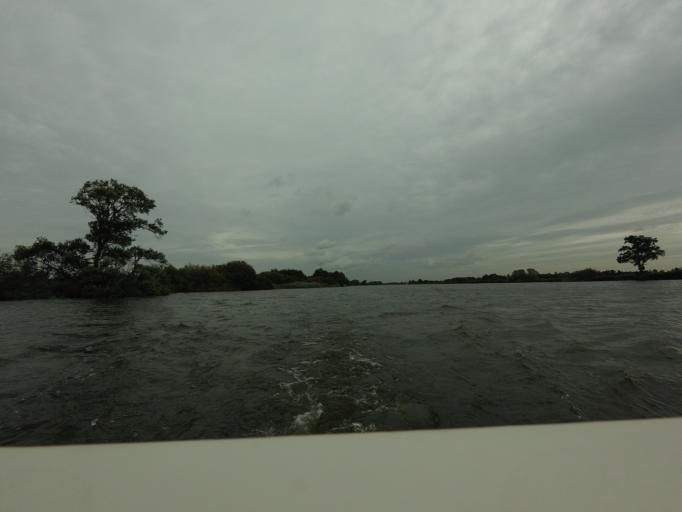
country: NL
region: Friesland
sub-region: Gemeente Boarnsterhim
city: Warten
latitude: 53.1194
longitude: 5.8996
